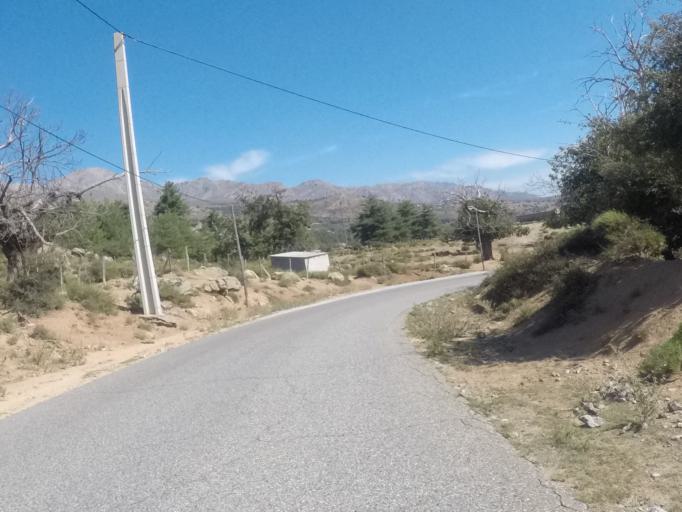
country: FR
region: Corsica
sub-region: Departement de la Haute-Corse
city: Corte
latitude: 42.3146
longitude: 8.9701
